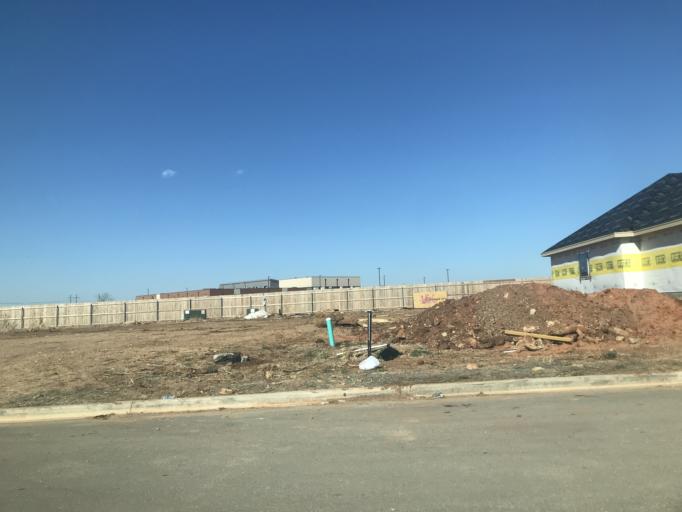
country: US
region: Texas
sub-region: Taylor County
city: Potosi
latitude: 32.3686
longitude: -99.7235
